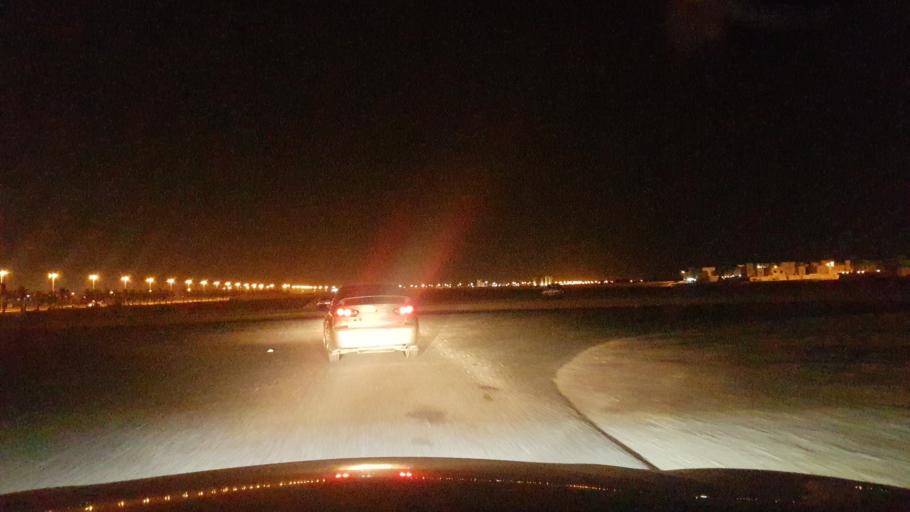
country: BH
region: Central Governorate
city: Dar Kulayb
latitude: 26.0484
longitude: 50.4982
